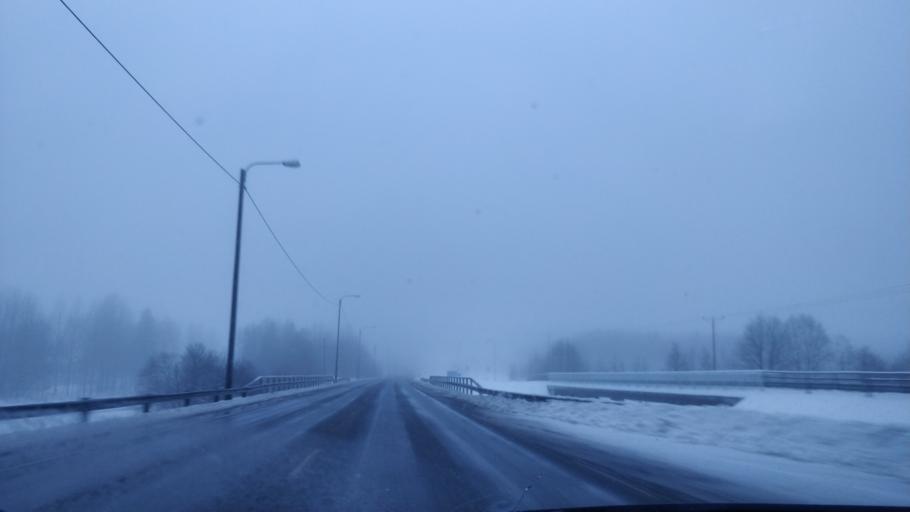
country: FI
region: Lapland
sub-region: Kemi-Tornio
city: Tervola
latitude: 66.1401
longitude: 24.9436
